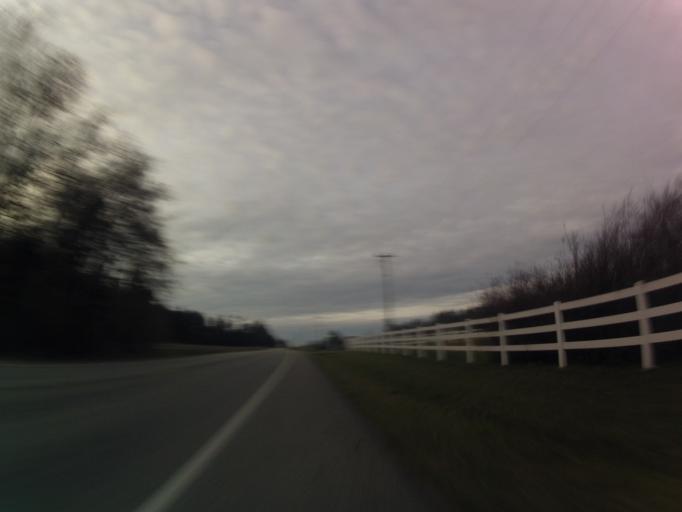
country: US
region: Washington
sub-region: Island County
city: Coupeville
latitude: 48.1724
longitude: -122.6803
